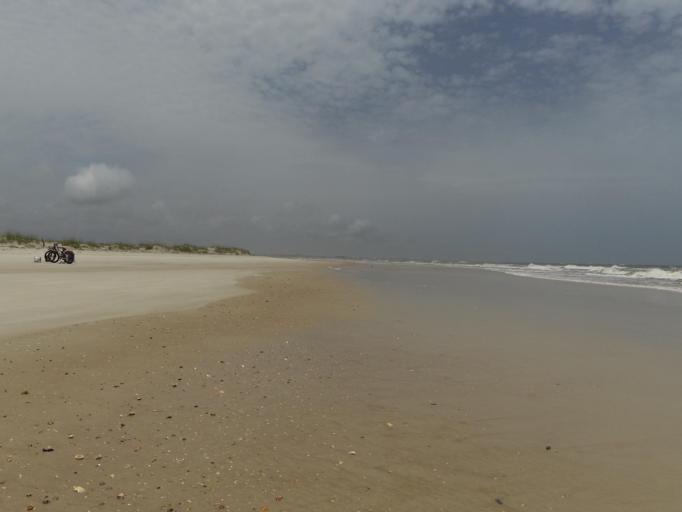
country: US
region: Florida
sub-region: Saint Johns County
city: Saint Augustine
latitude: 29.9046
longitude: -81.2775
